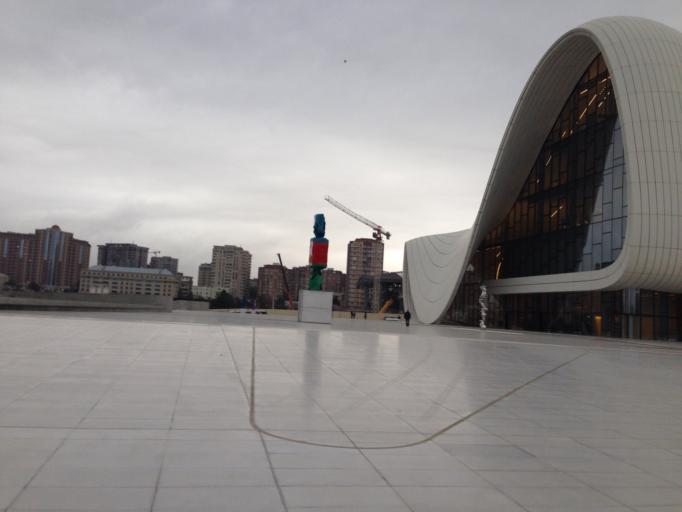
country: AZ
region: Baki
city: Baku
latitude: 40.3947
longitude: 49.8674
